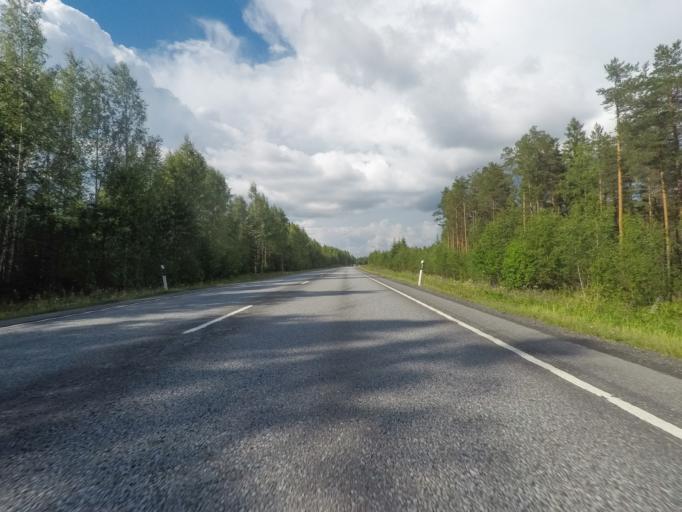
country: FI
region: Southern Savonia
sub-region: Mikkeli
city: Ristiina
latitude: 61.6032
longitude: 27.0434
